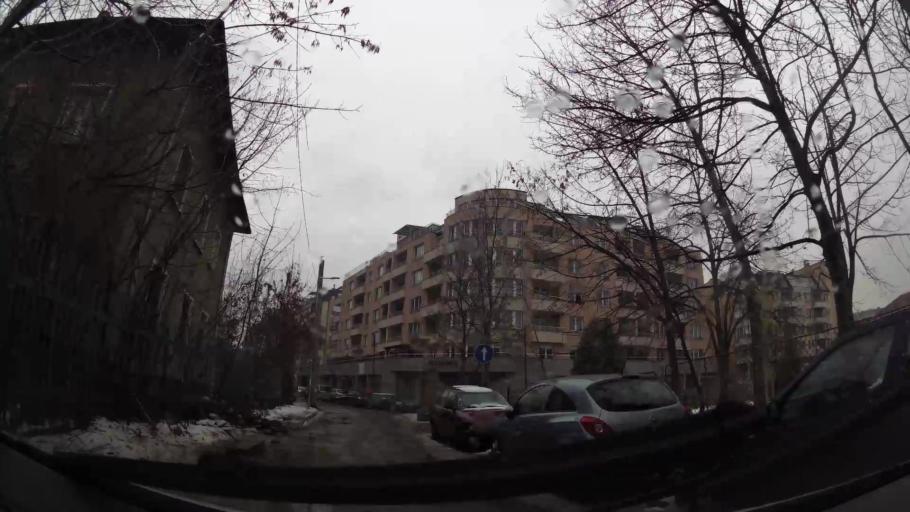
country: BG
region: Sofia-Capital
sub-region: Stolichna Obshtina
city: Sofia
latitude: 42.6654
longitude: 23.2968
